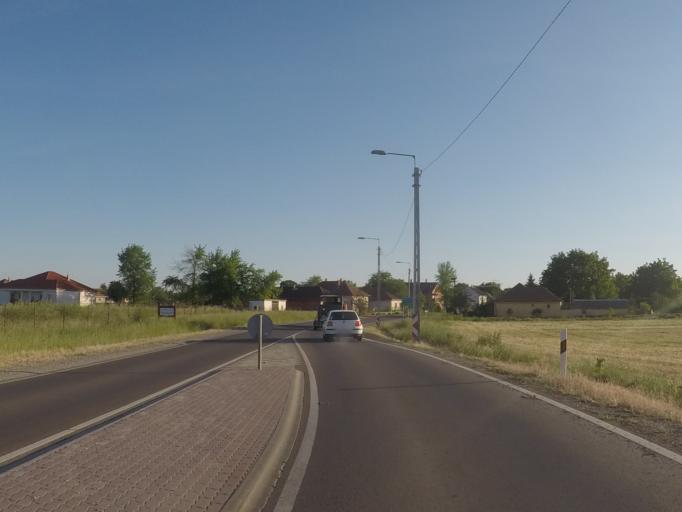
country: HU
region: Heves
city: Erdotelek
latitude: 47.6590
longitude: 20.3471
